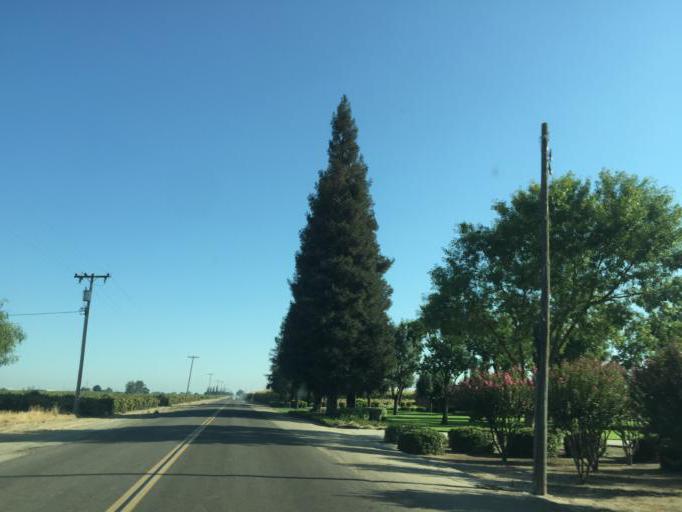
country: US
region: California
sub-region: Fresno County
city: Kingsburg
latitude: 36.4857
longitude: -119.5283
